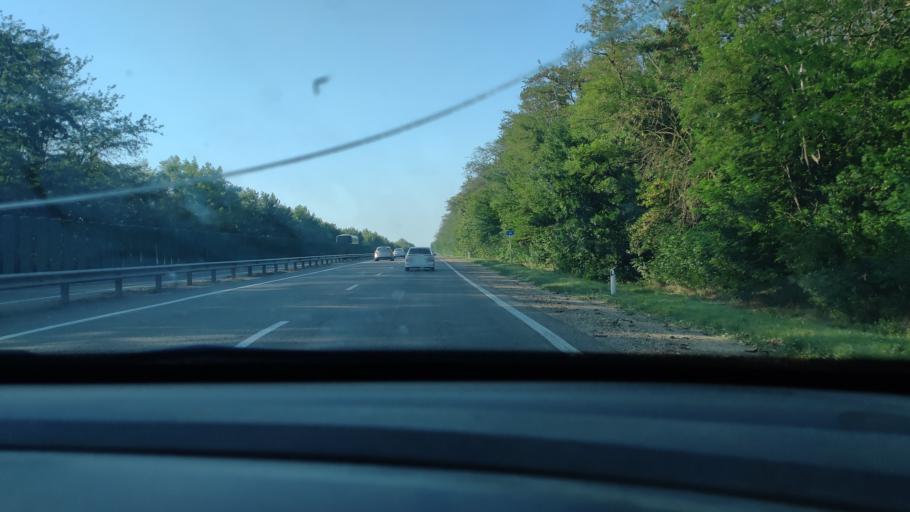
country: RU
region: Krasnodarskiy
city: Timashevsk
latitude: 45.5290
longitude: 38.9410
